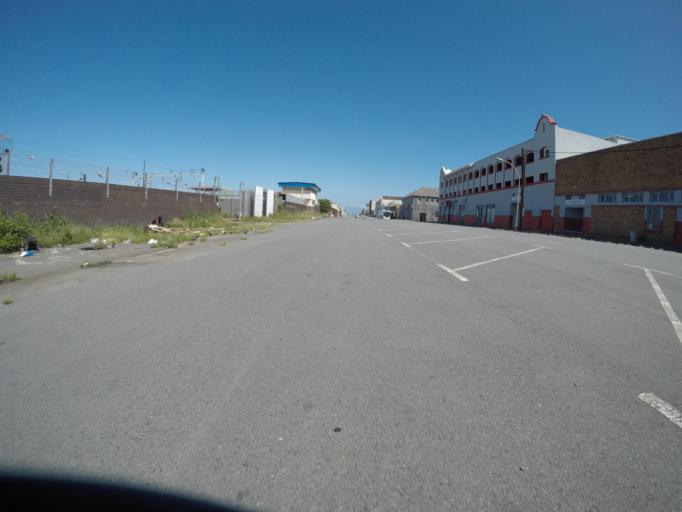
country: ZA
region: Eastern Cape
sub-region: Buffalo City Metropolitan Municipality
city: East London
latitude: -33.0136
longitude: 27.9062
